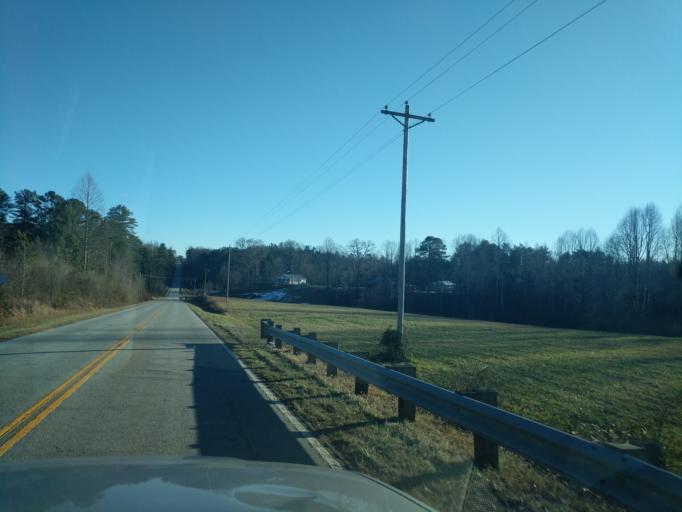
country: US
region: Georgia
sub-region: Rabun County
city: Clayton
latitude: 34.7873
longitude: -83.2651
